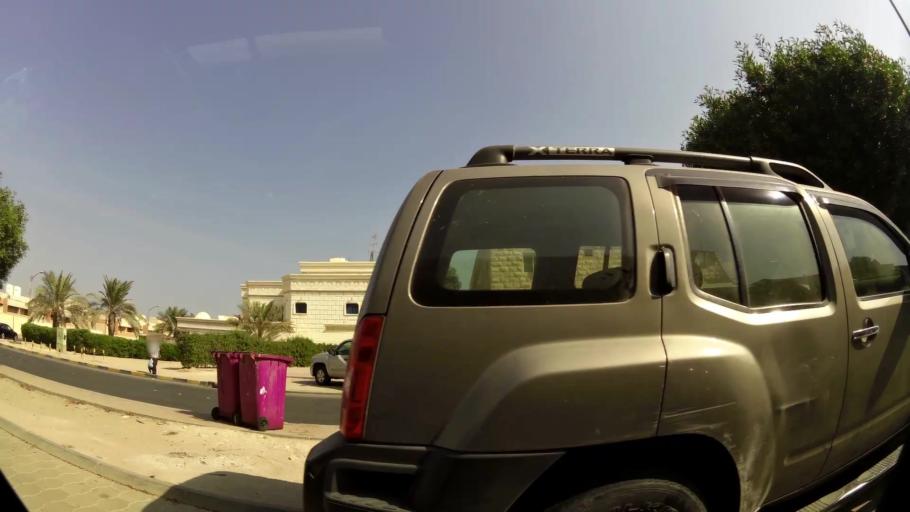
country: KW
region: Al Ahmadi
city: Al Fahahil
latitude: 29.0832
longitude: 48.1184
